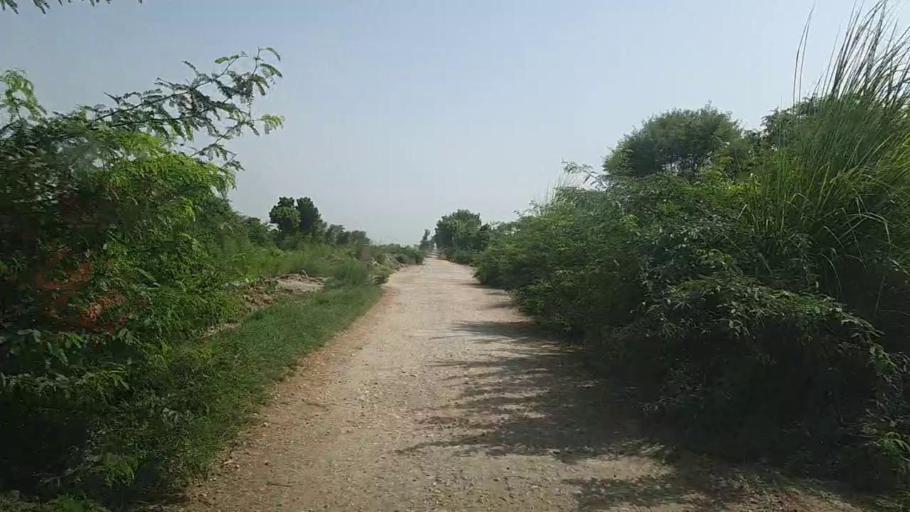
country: PK
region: Sindh
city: Pad Idan
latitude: 26.7859
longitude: 68.3252
